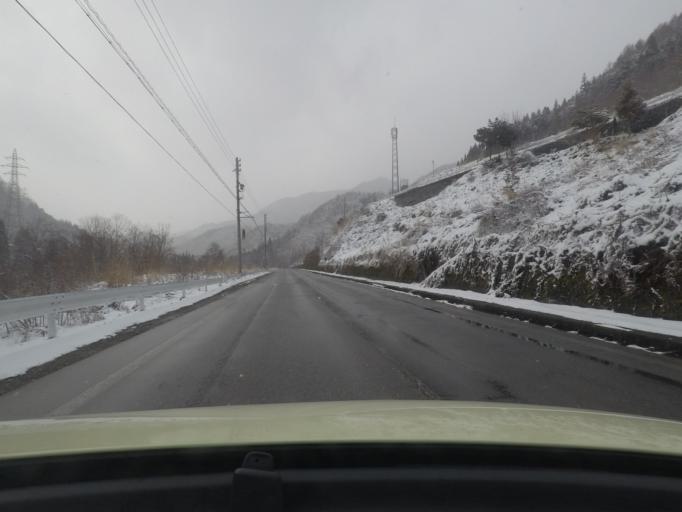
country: JP
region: Gifu
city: Takayama
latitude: 36.1745
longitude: 137.4206
